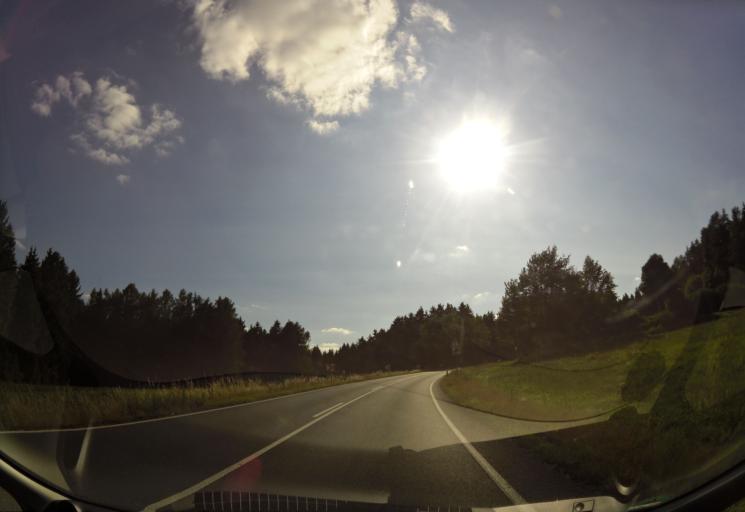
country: DE
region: Thuringia
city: Tanna
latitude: 50.4431
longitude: 11.8371
